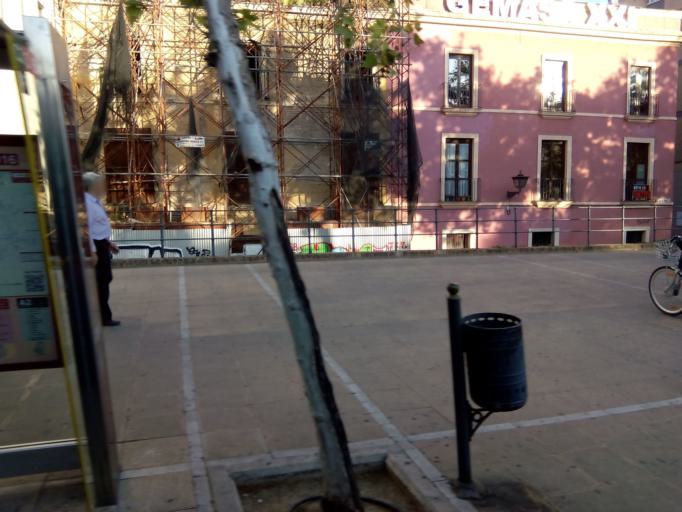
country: ES
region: Andalusia
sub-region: Provincia de Sevilla
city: Sevilla
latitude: 37.4005
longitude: -5.9985
